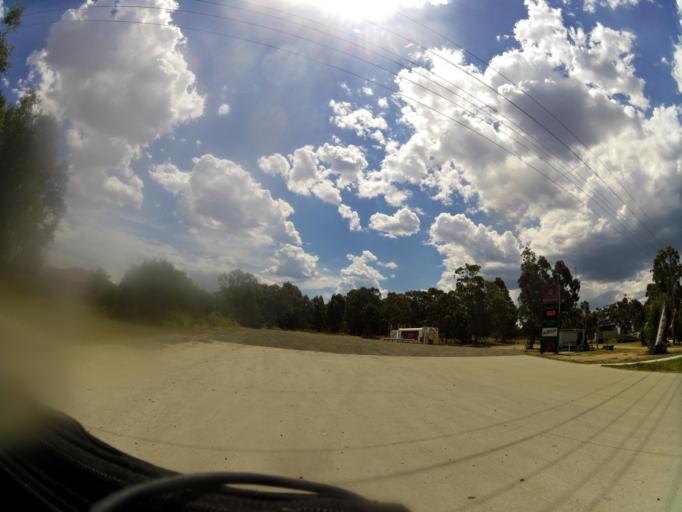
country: AU
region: Victoria
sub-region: Wellington
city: Heyfield
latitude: -37.9791
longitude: 146.7839
